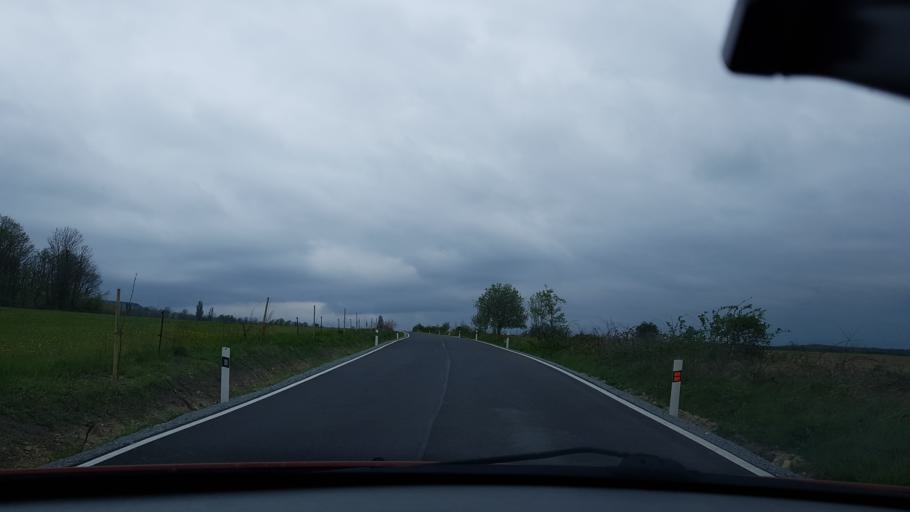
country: PL
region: Opole Voivodeship
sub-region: Powiat nyski
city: Kamienica
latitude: 50.4339
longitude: 16.9465
